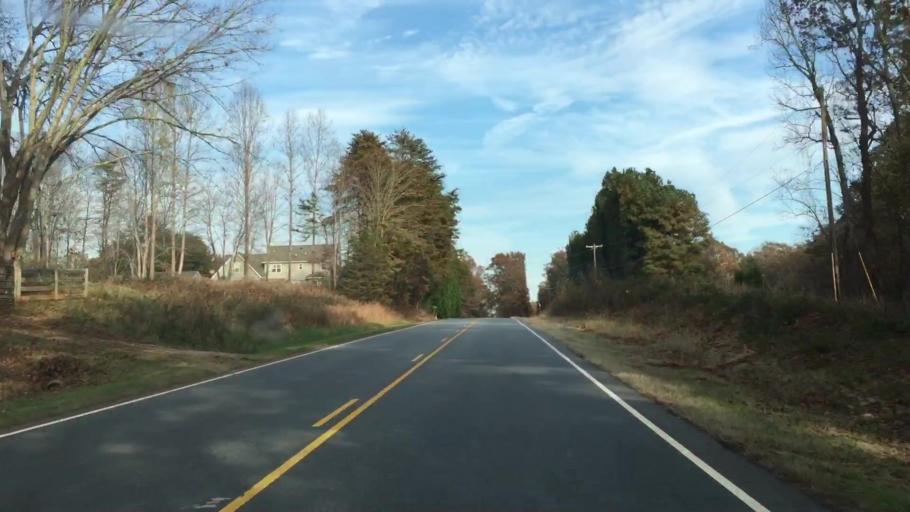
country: US
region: North Carolina
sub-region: Guilford County
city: Summerfield
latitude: 36.2658
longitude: -79.8534
